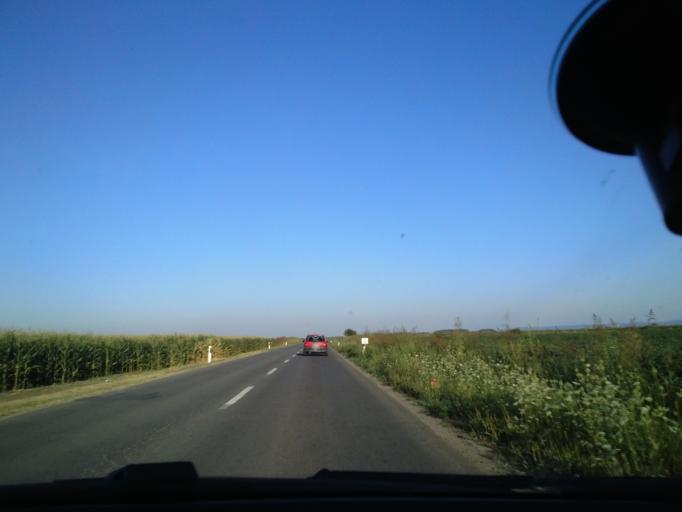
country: RS
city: Maglic
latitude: 45.3855
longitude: 19.5034
